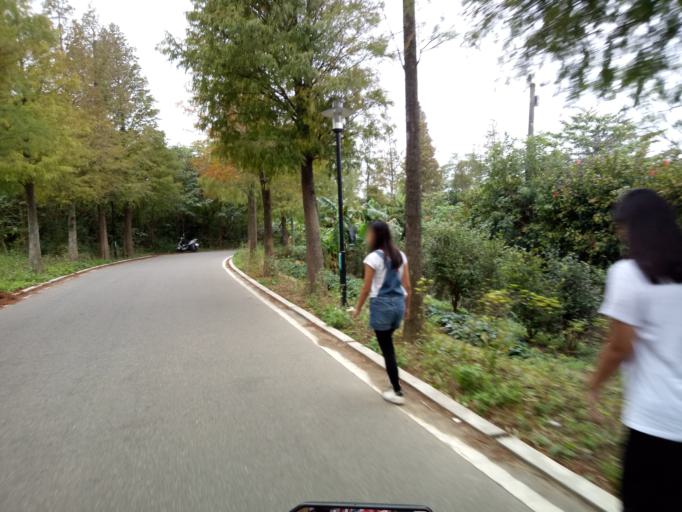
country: TW
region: Taiwan
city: Daxi
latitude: 24.8742
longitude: 121.2553
